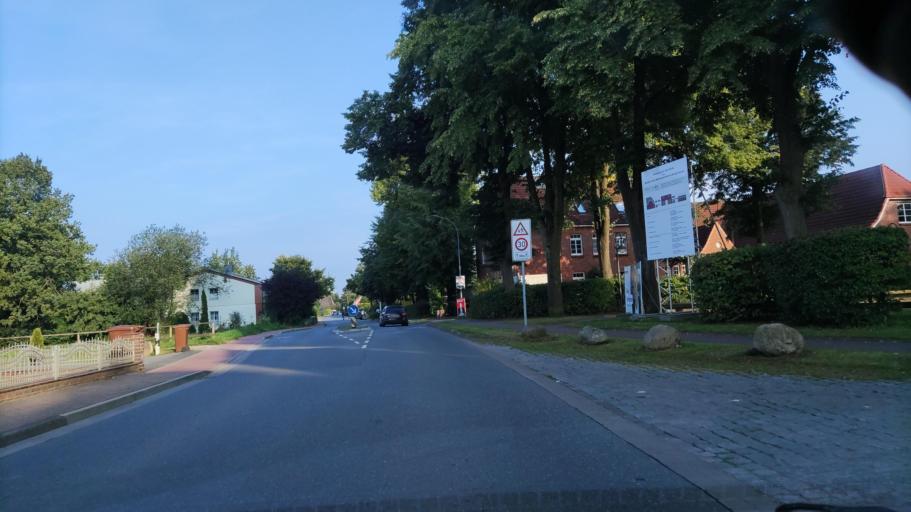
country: DE
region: Schleswig-Holstein
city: Itzstedt
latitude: 53.8246
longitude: 10.1495
